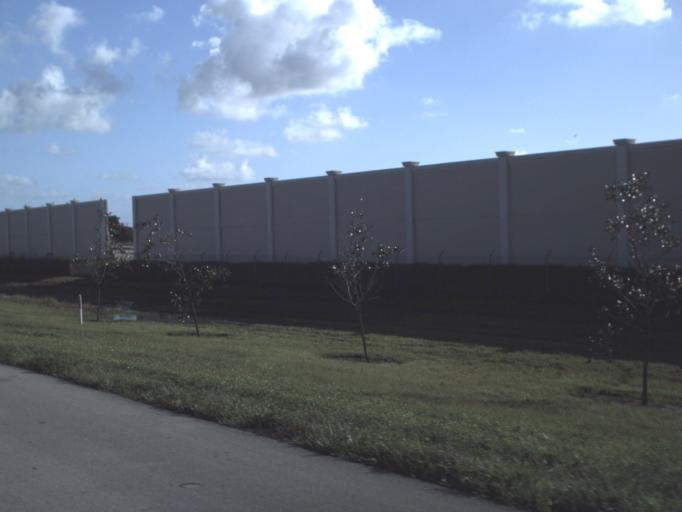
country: US
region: Florida
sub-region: Broward County
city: Lauderdale Lakes
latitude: 26.1828
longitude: -80.2177
